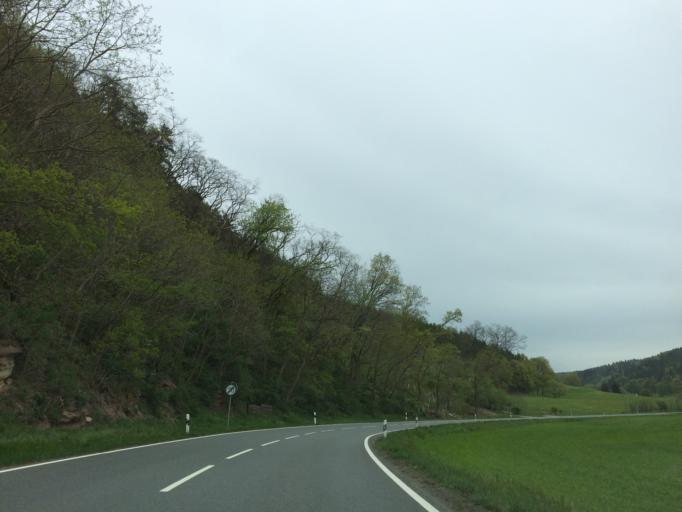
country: DE
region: Thuringia
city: Freienorla
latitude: 50.7626
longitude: 11.5436
